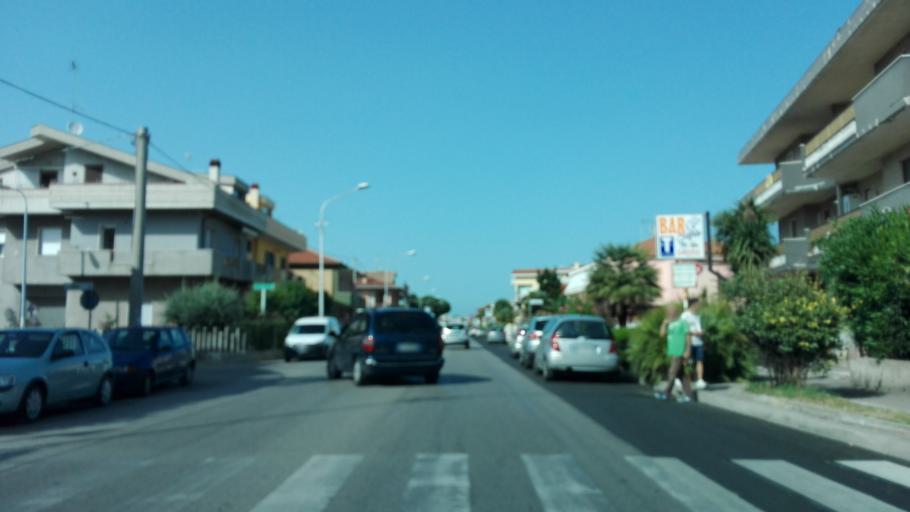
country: IT
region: Abruzzo
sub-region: Provincia di Pescara
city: Montesilvano Marina
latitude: 42.5074
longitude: 14.1402
